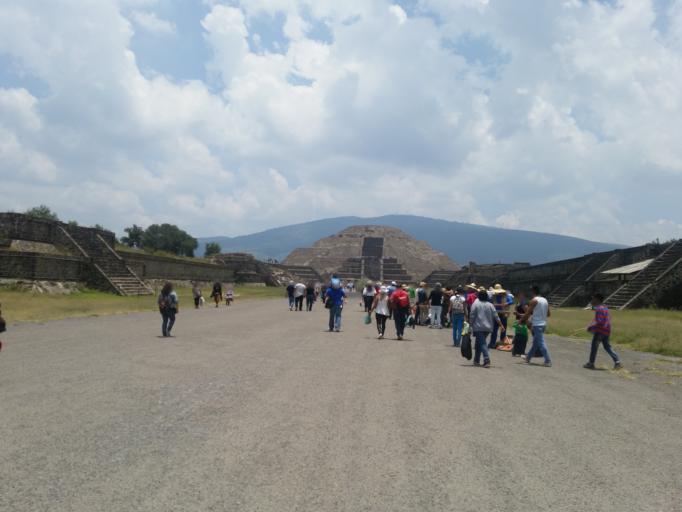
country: MX
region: Morelos
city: San Martin de las Piramides
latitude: 19.6951
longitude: -98.8452
